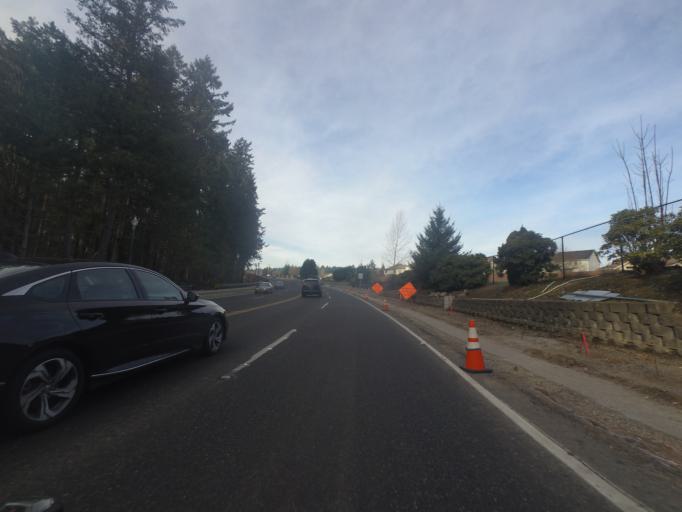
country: US
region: Washington
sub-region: Pierce County
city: Lakewood
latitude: 47.1984
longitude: -122.5230
